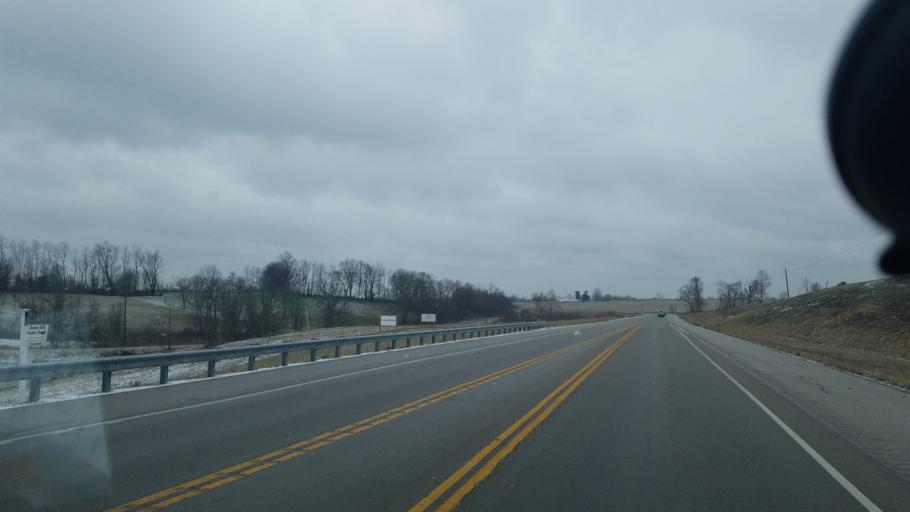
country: US
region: Kentucky
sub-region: Montgomery County
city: Mount Sterling
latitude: 38.2001
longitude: -83.9348
